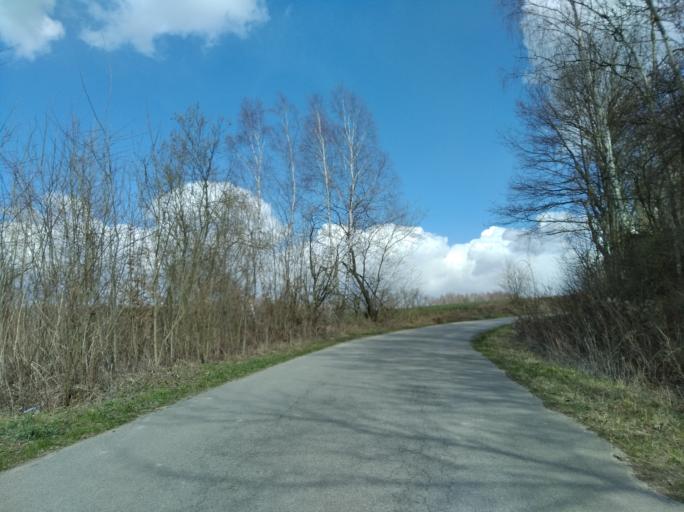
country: PL
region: Subcarpathian Voivodeship
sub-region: Powiat strzyzowski
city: Wisniowa
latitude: 49.9251
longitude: 21.7032
